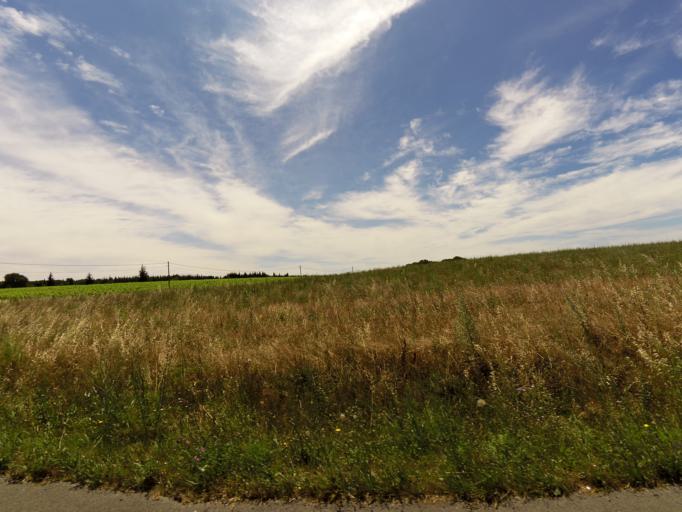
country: FR
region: Languedoc-Roussillon
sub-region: Departement du Gard
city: Milhaud
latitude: 43.7775
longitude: 4.3396
